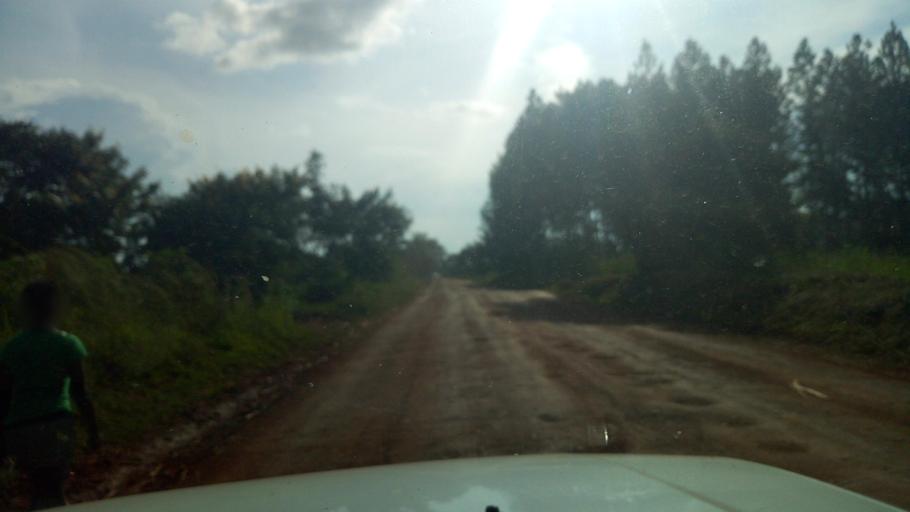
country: UG
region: Western Region
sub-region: Masindi District
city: Masindi
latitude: 1.6747
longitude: 31.6633
